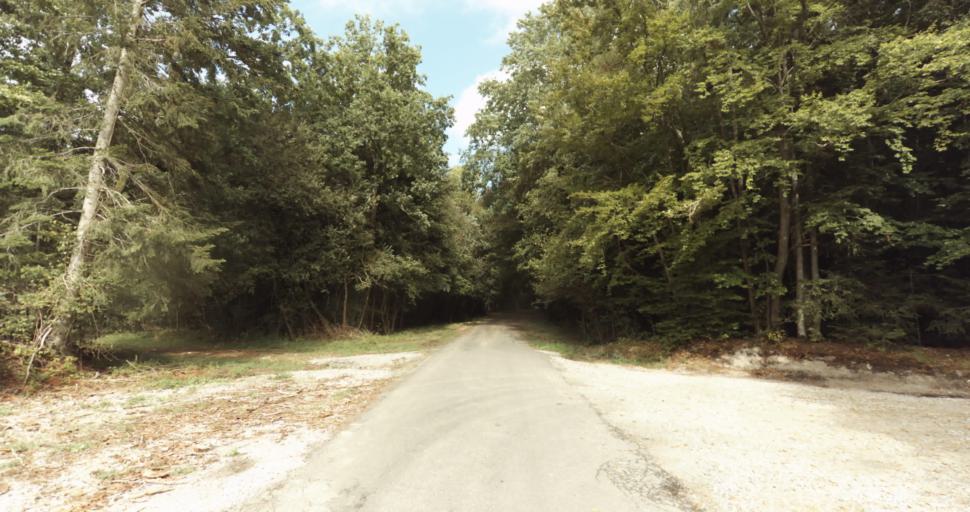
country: FR
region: Lower Normandy
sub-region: Departement de l'Orne
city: Gace
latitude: 48.7809
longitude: 0.3220
